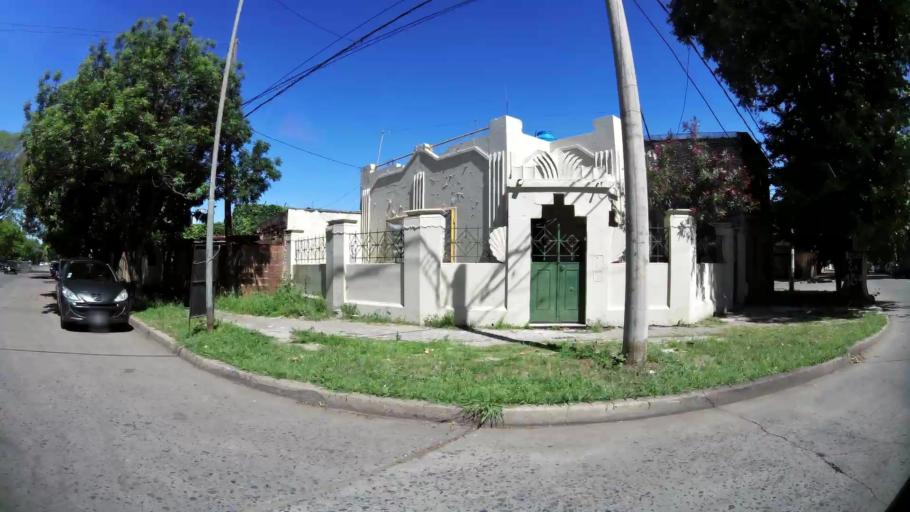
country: AR
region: Santa Fe
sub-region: Departamento de Rosario
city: Rosario
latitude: -32.9338
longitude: -60.6806
